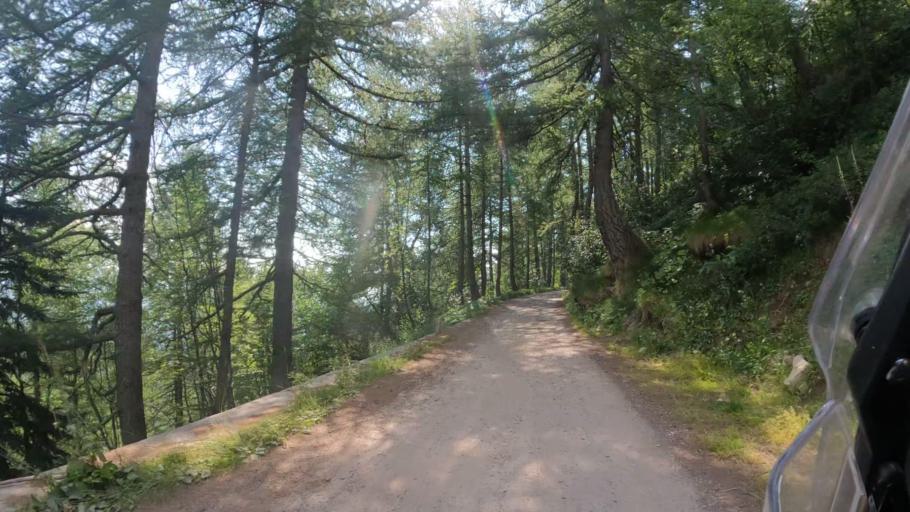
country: IT
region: Piedmont
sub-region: Provincia di Cuneo
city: Briga Alta
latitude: 44.1081
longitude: 7.7051
